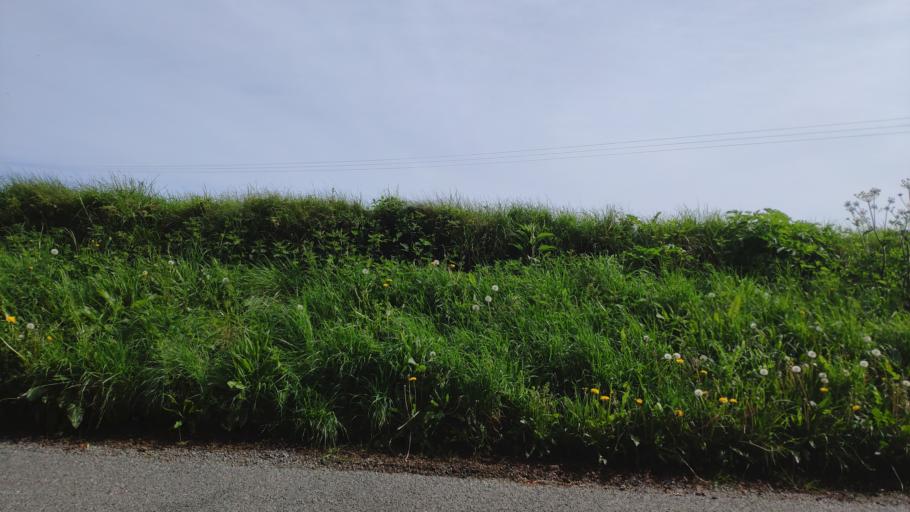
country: IE
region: Munster
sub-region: County Cork
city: Blarney
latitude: 51.9543
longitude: -8.5060
